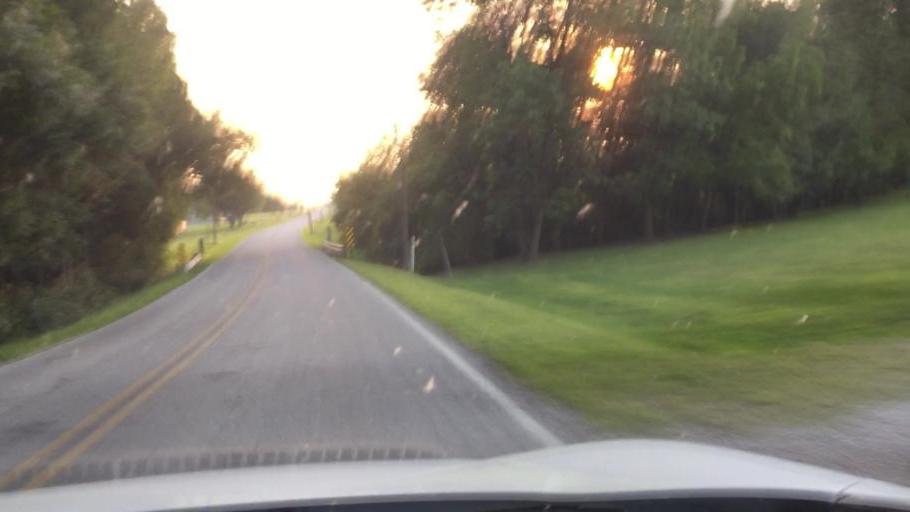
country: US
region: Ohio
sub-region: Madison County
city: Choctaw Lake
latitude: 39.9476
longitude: -83.5097
